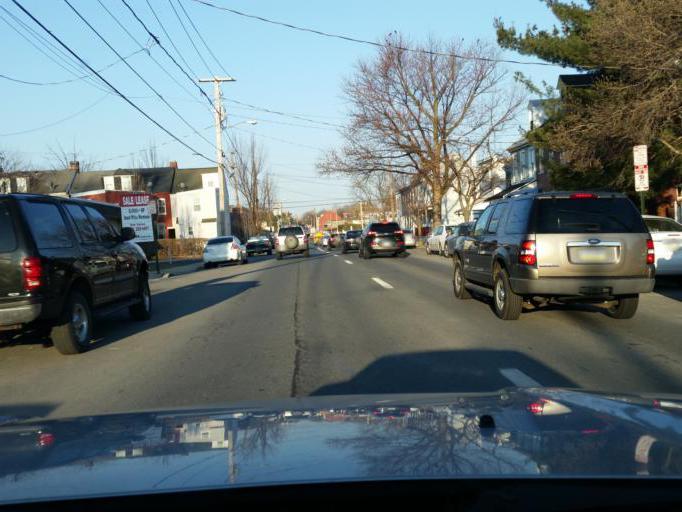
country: US
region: Pennsylvania
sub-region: Lancaster County
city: Lancaster
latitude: 40.0441
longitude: -76.2929
